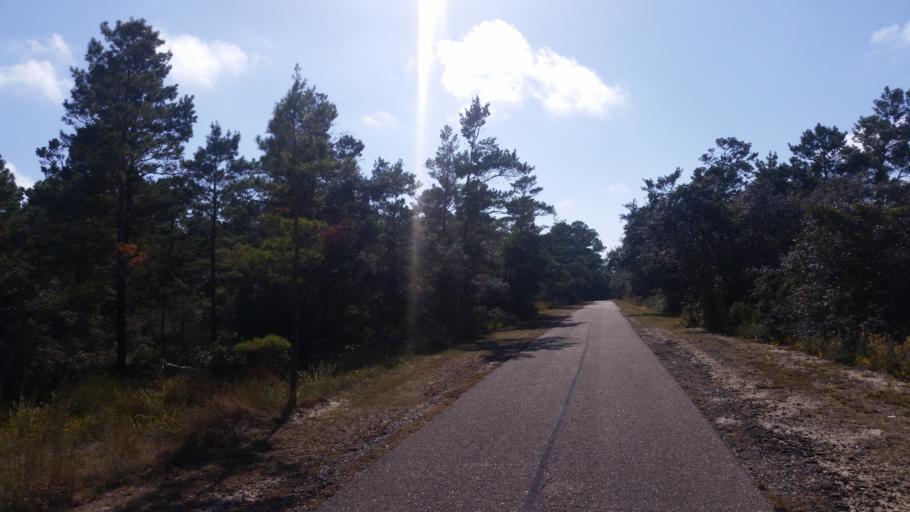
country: US
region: Alabama
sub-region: Baldwin County
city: Orange Beach
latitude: 30.2751
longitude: -87.6005
